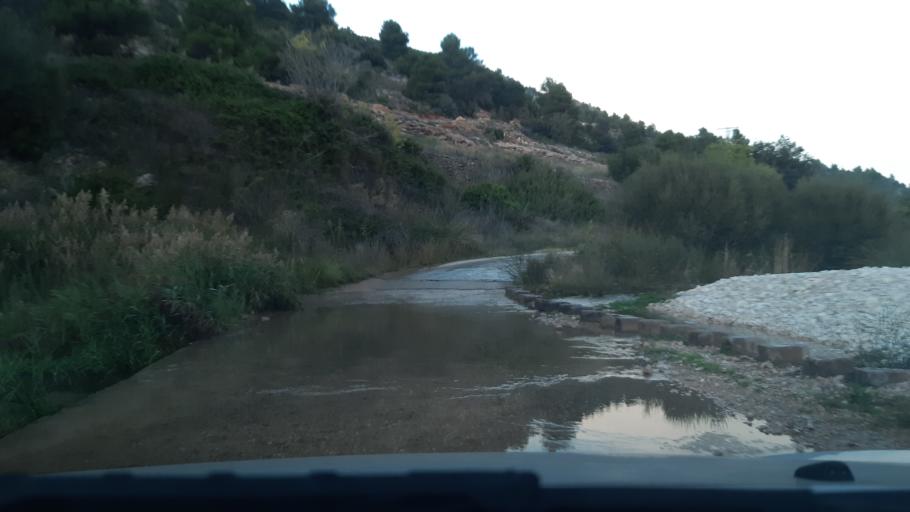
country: ES
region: Aragon
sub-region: Provincia de Teruel
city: Valderrobres
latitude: 40.8405
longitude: 0.1943
